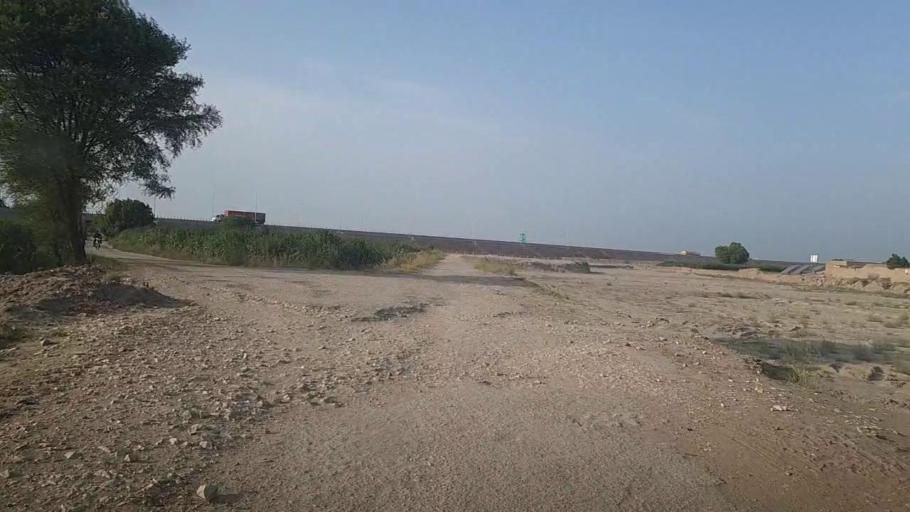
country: PK
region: Sindh
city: Ubauro
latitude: 28.3311
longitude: 69.7983
